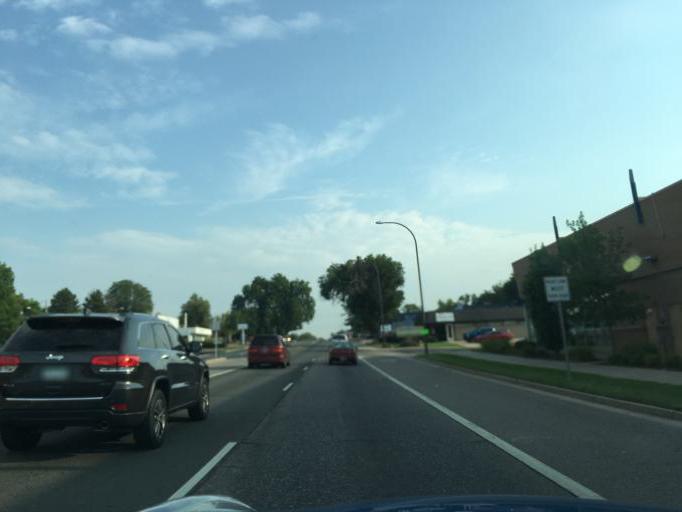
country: US
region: Colorado
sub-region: Jefferson County
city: Edgewater
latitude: 39.7433
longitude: -105.0814
